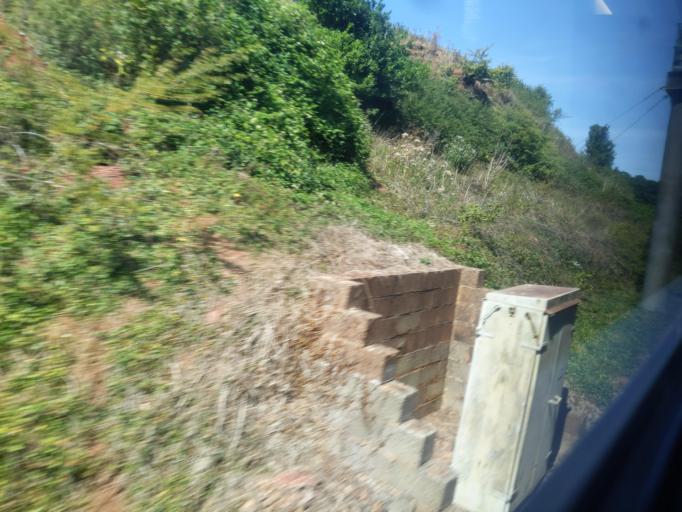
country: GB
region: England
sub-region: Devon
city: Ipplepen
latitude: 50.4762
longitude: -3.6360
